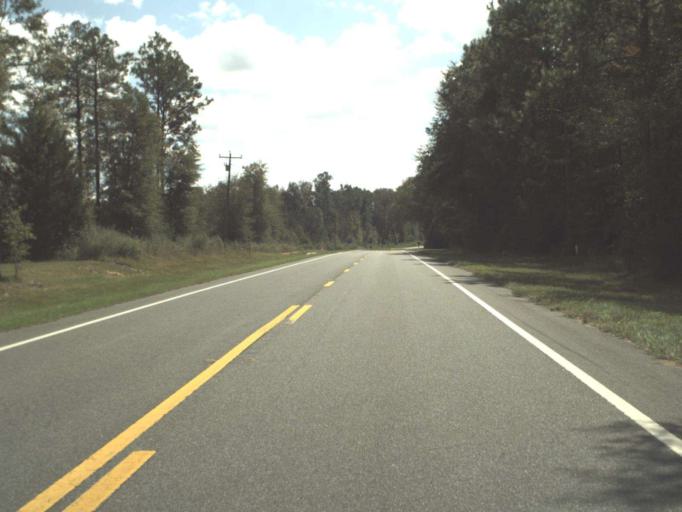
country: US
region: Alabama
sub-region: Geneva County
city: Geneva
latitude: 30.9410
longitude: -85.9724
